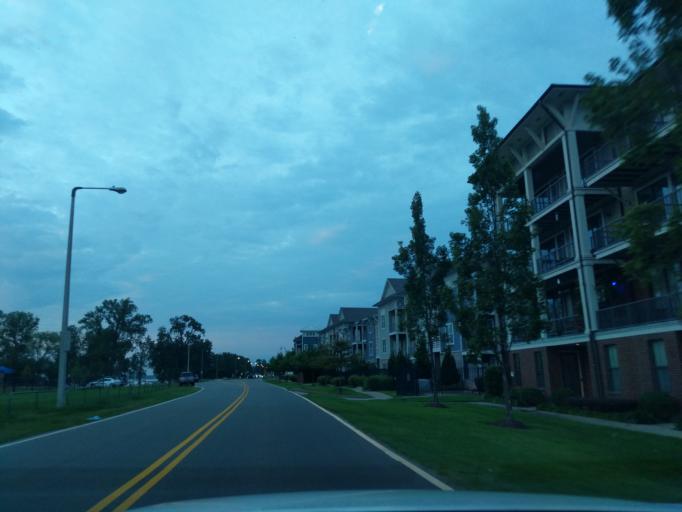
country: US
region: Tennessee
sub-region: Shelby County
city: Memphis
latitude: 35.1571
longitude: -90.0564
